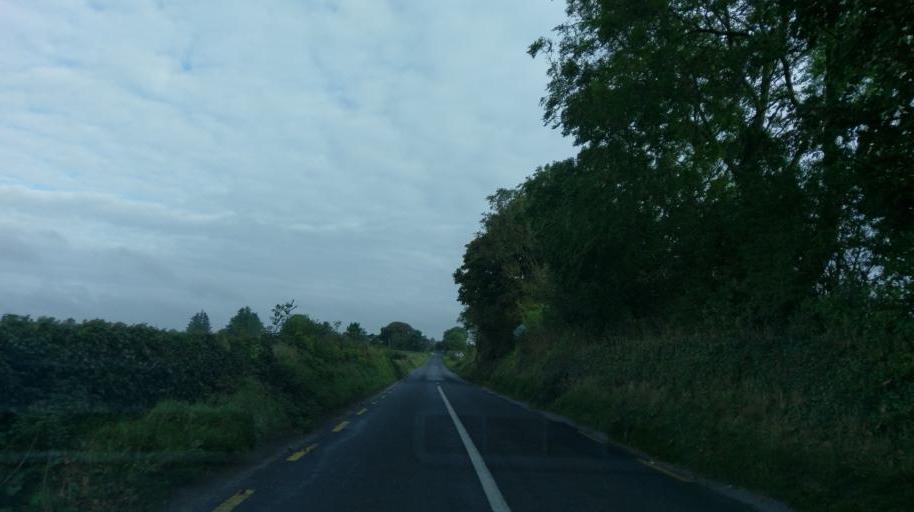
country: IE
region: Connaught
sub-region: County Galway
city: Athenry
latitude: 53.3150
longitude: -8.7319
